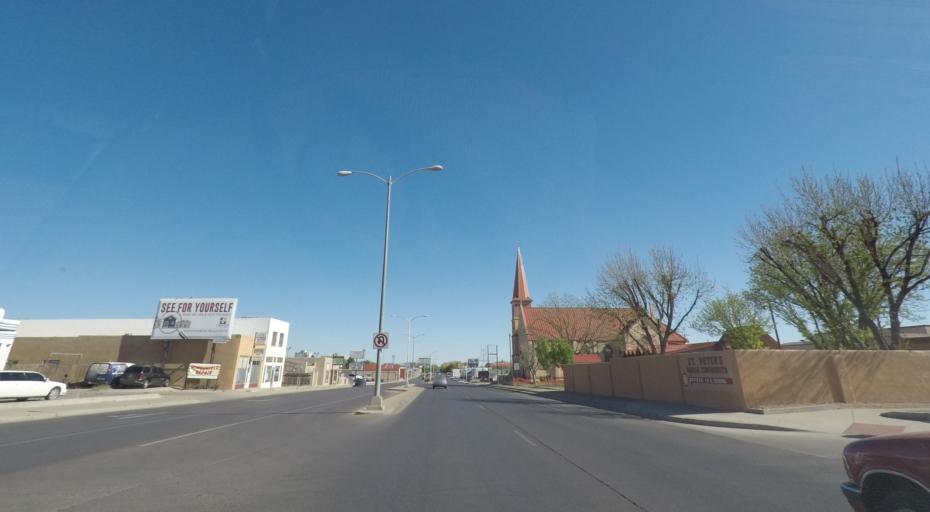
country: US
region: New Mexico
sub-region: Chaves County
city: Roswell
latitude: 33.3846
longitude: -104.5227
